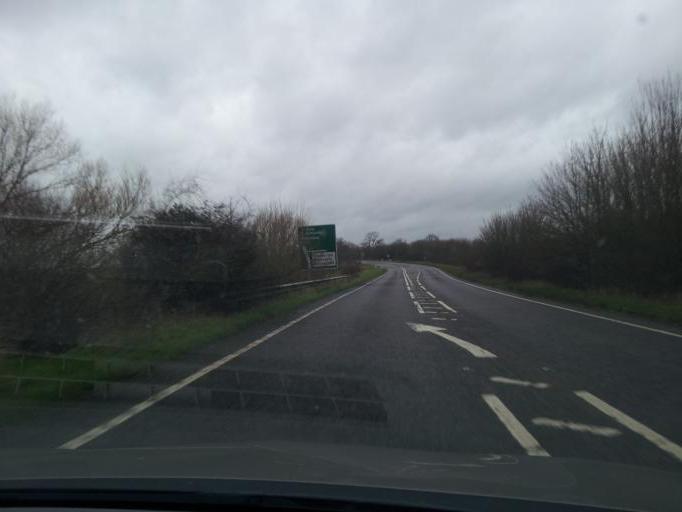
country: GB
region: England
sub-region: Suffolk
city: Botesdale
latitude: 52.3333
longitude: 0.9860
